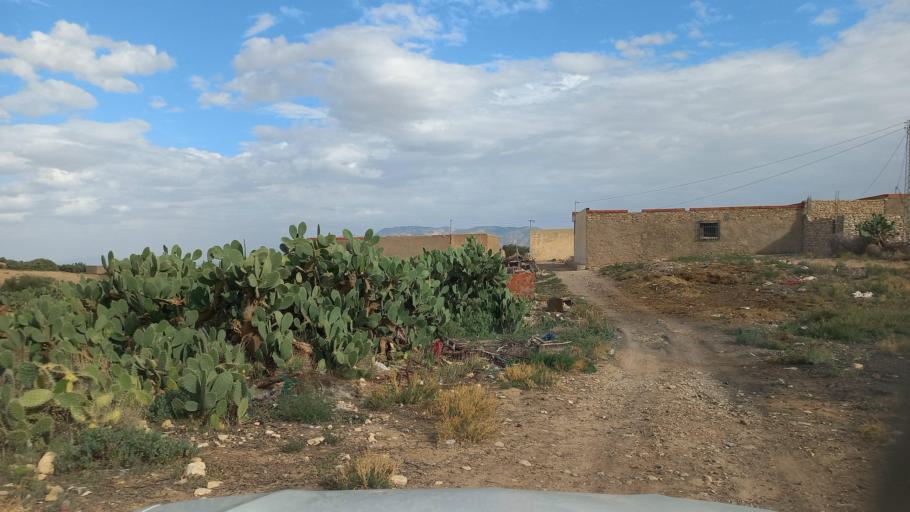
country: TN
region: Al Qasrayn
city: Sbiba
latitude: 35.4517
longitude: 9.0870
